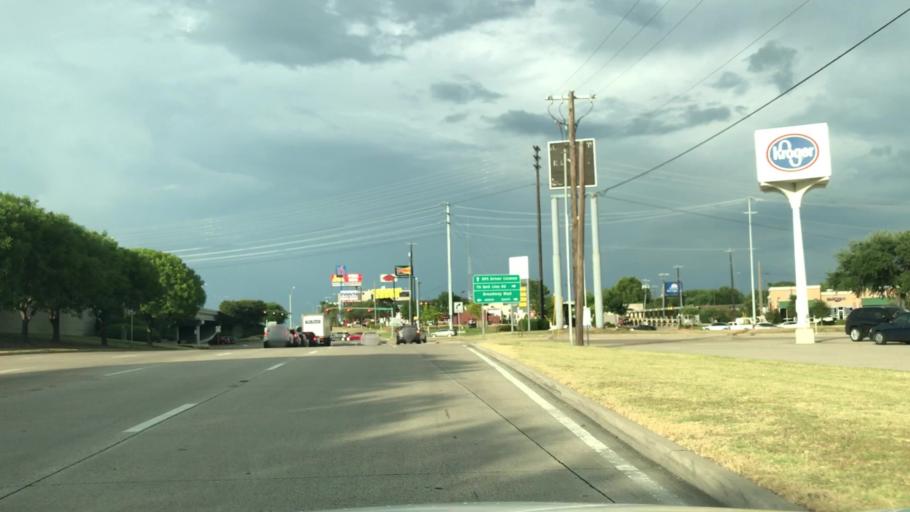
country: US
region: Texas
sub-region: Dallas County
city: Sunnyvale
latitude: 32.8383
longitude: -96.5974
